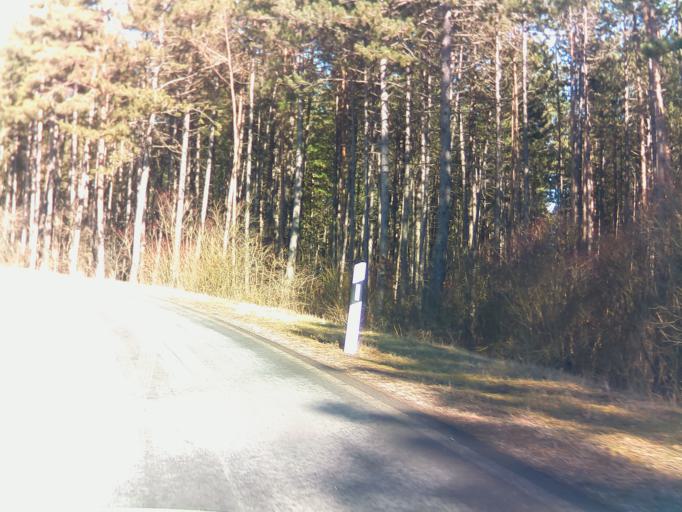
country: DE
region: Bavaria
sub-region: Regierungsbezirk Unterfranken
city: Burglauer
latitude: 50.2453
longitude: 10.1755
